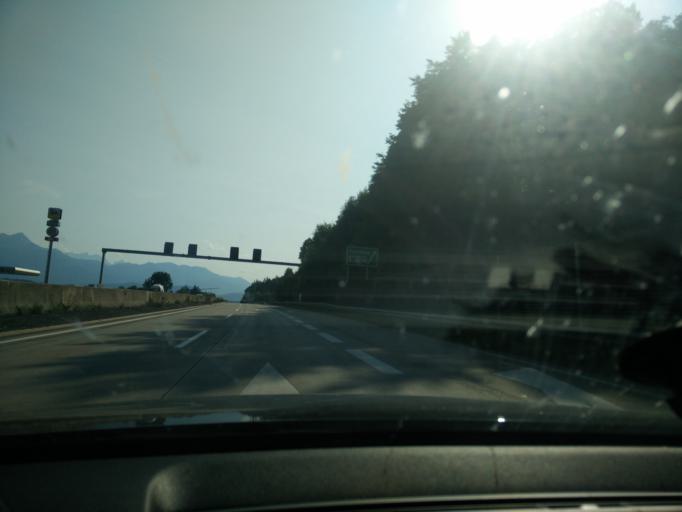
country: AT
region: Carinthia
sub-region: Politischer Bezirk Klagenfurt Land
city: Schiefling am See
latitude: 46.6314
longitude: 14.0955
